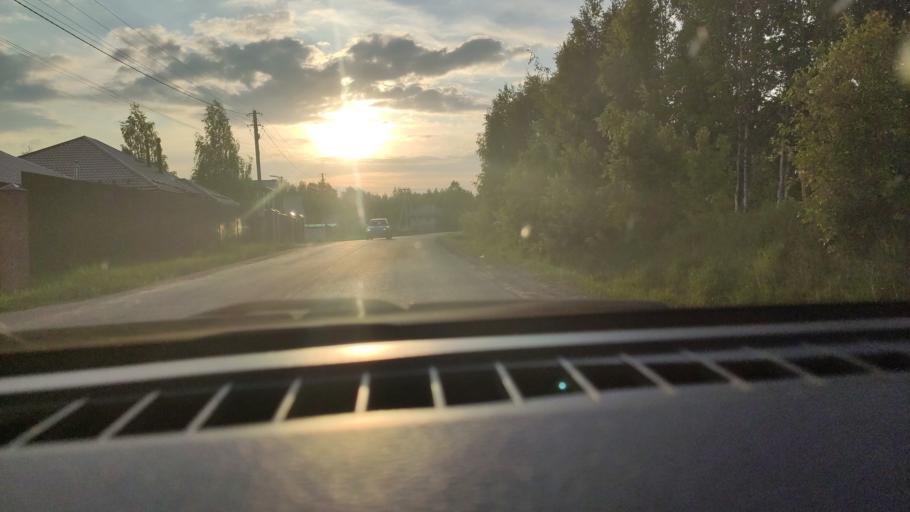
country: RU
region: Perm
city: Kondratovo
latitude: 58.0575
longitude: 56.0078
